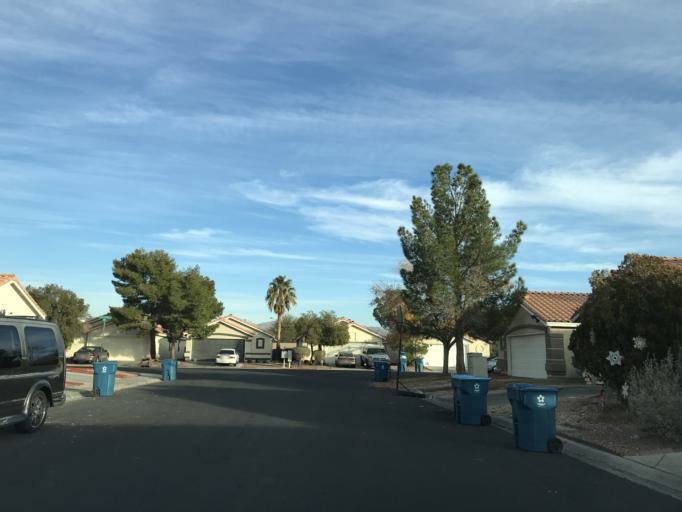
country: US
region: Nevada
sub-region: Clark County
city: Nellis Air Force Base
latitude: 36.2452
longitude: -115.0572
